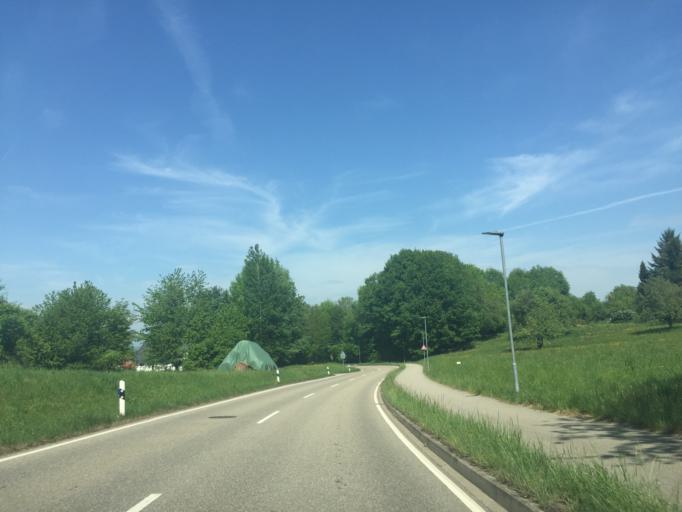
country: DE
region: Baden-Wuerttemberg
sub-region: Karlsruhe Region
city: Malsch
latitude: 48.8722
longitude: 8.3457
